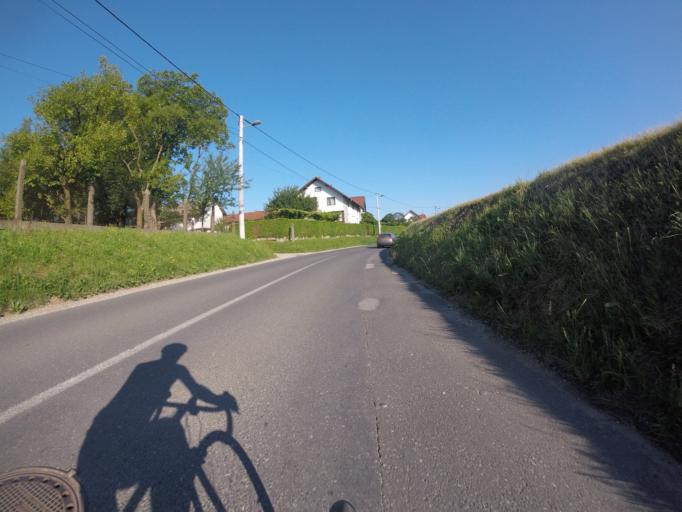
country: HR
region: Grad Zagreb
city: Zadvorsko
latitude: 45.7249
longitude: 15.9198
